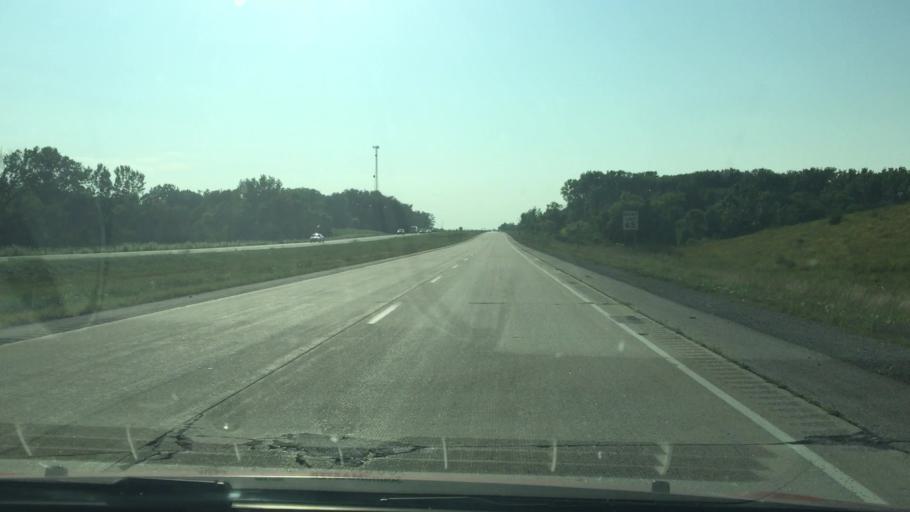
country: US
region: Iowa
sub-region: Scott County
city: Blue Grass
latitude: 41.5178
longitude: -90.8445
